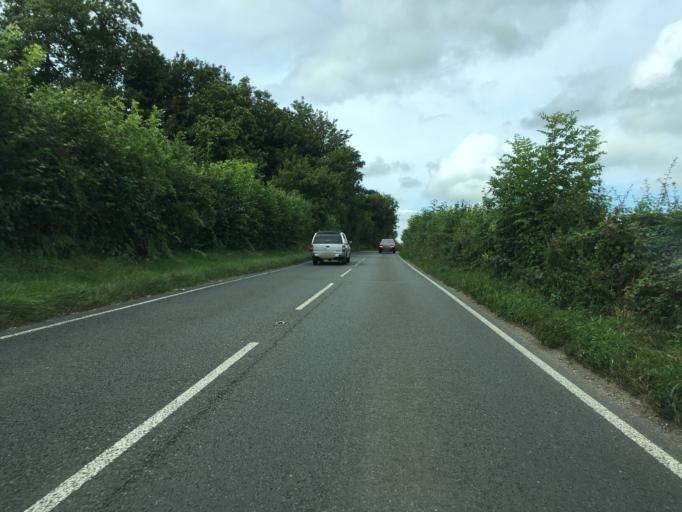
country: GB
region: England
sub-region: Kent
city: Royal Tunbridge Wells
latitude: 51.1249
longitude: 0.1943
